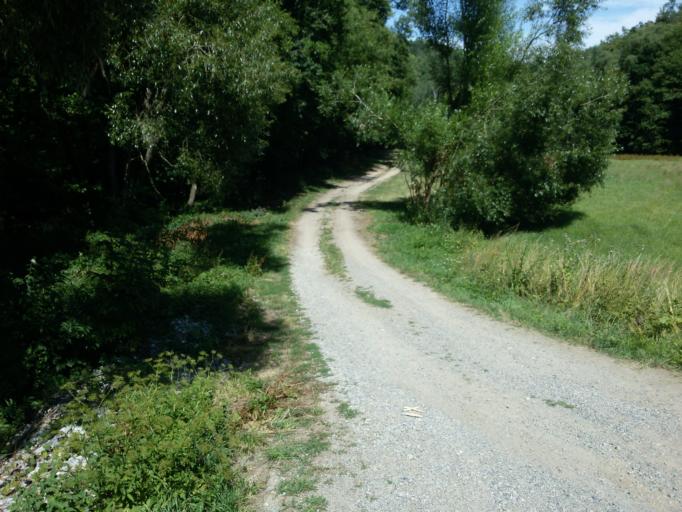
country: CZ
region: Vysocina
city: Rouchovany
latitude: 49.0407
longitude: 16.0505
